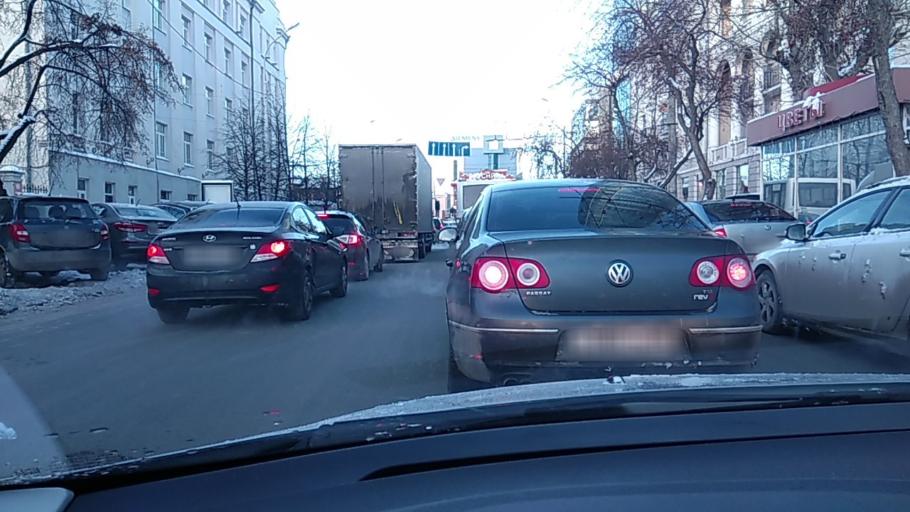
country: RU
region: Sverdlovsk
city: Yekaterinburg
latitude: 56.8347
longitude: 60.6143
